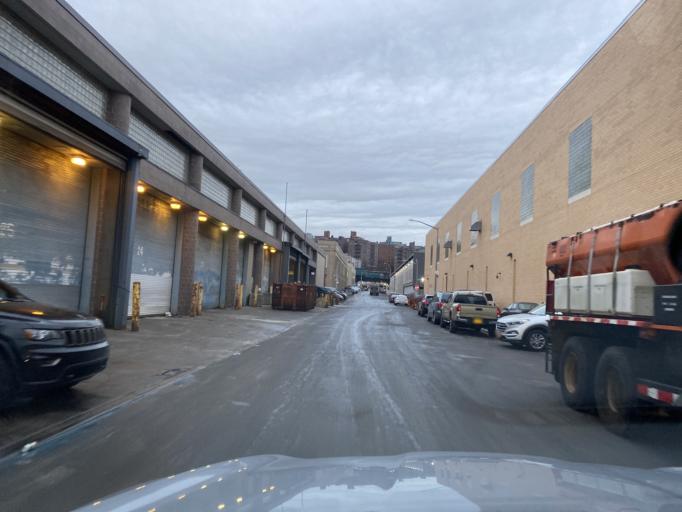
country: US
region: New York
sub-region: New York County
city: Inwood
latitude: 40.8690
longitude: -73.9117
